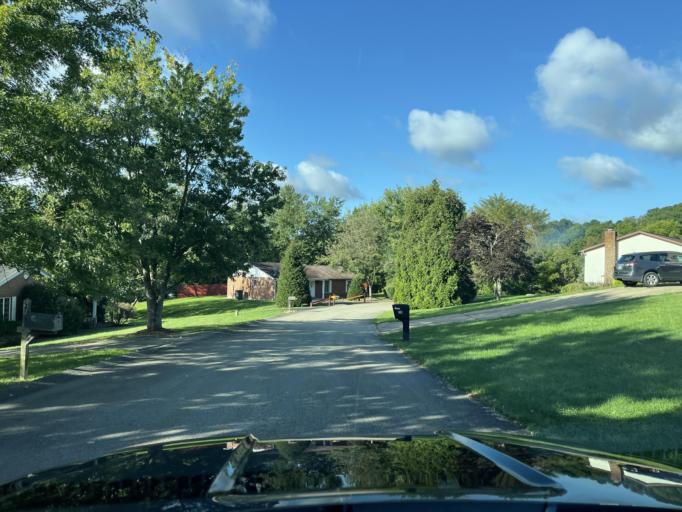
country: US
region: Pennsylvania
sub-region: Fayette County
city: South Uniontown
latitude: 39.8837
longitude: -79.7547
